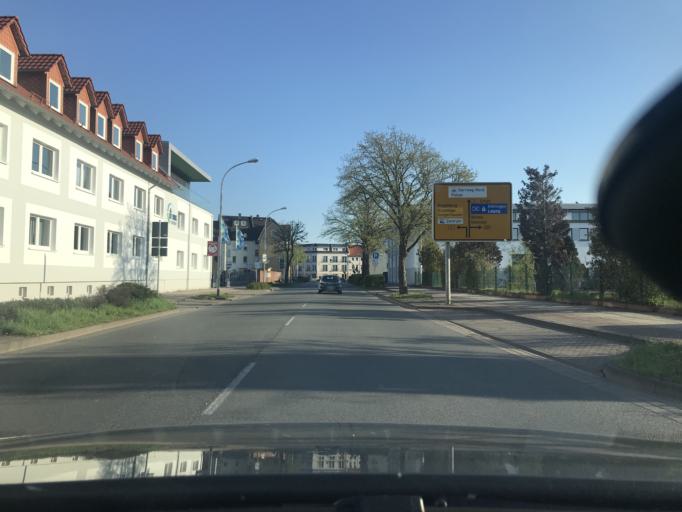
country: DE
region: Thuringia
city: Nordhausen
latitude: 51.4981
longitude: 10.7823
